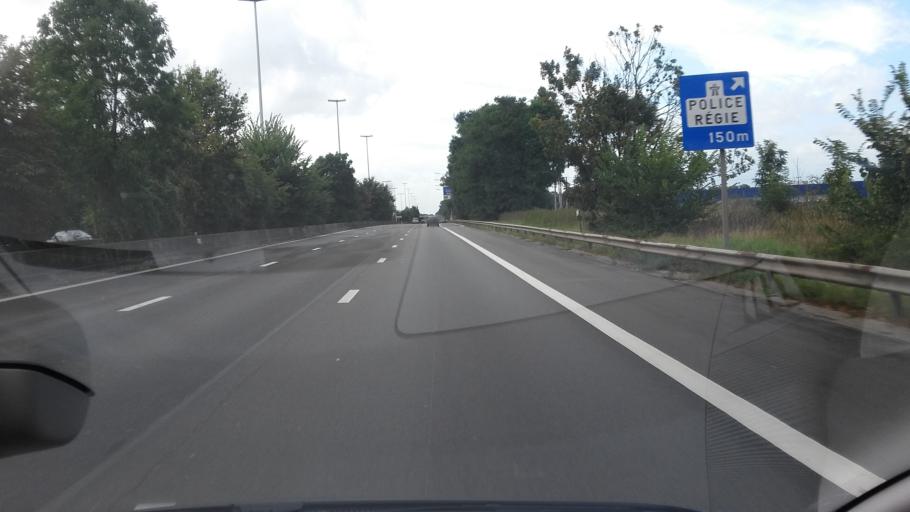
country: BE
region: Wallonia
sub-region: Province de Liege
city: Awans
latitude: 50.6756
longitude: 5.4673
